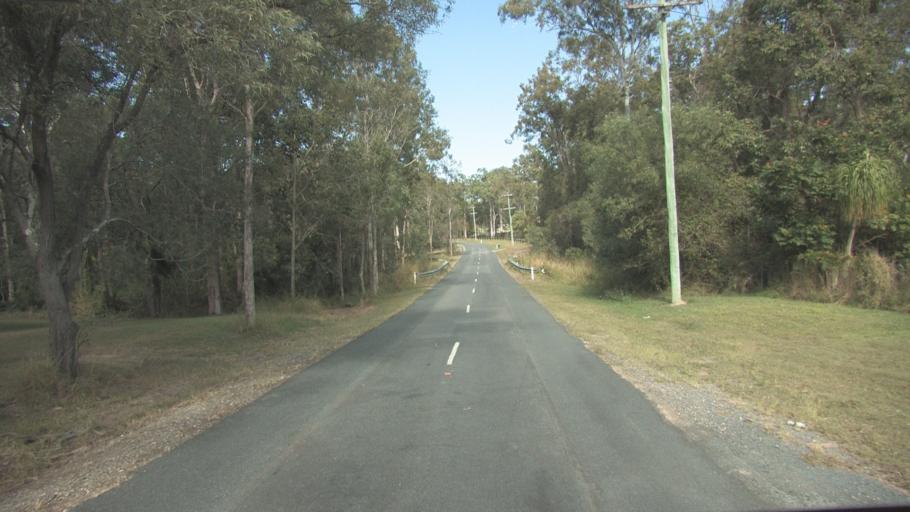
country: AU
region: Queensland
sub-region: Logan
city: North Maclean
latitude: -27.7501
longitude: 152.9735
